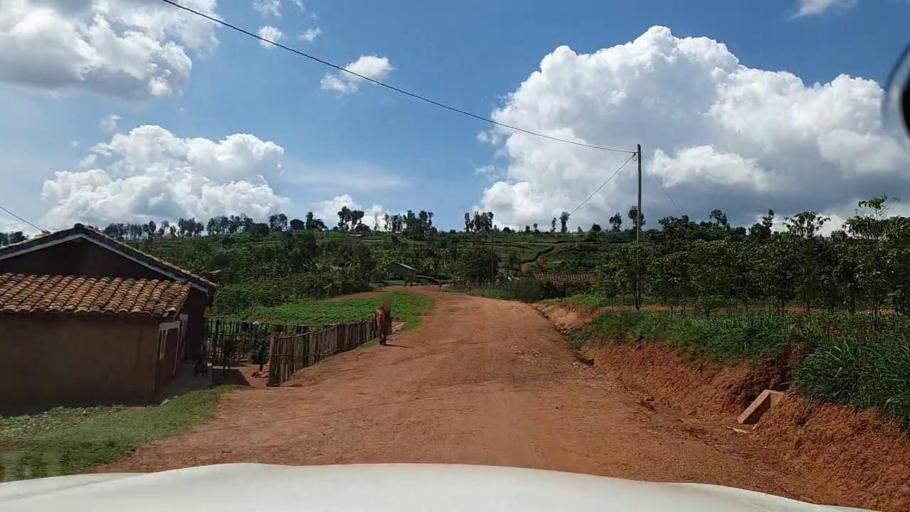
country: RW
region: Southern Province
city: Butare
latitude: -2.7454
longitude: 29.7030
